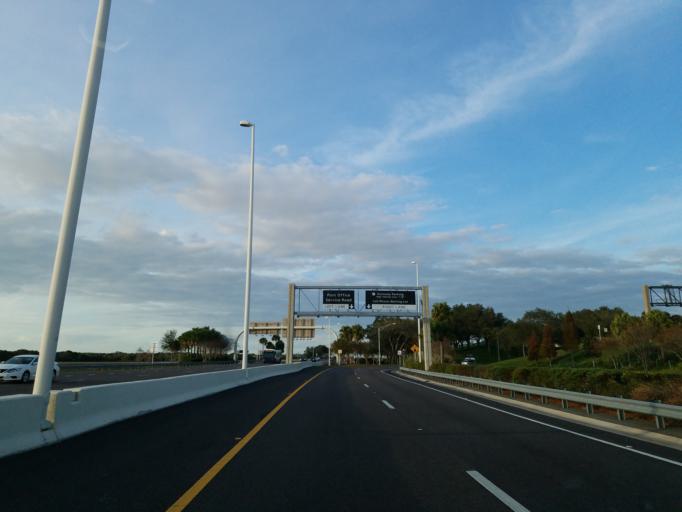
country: US
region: Florida
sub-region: Hillsborough County
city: Town 'n' Country
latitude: 27.9652
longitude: -82.5394
